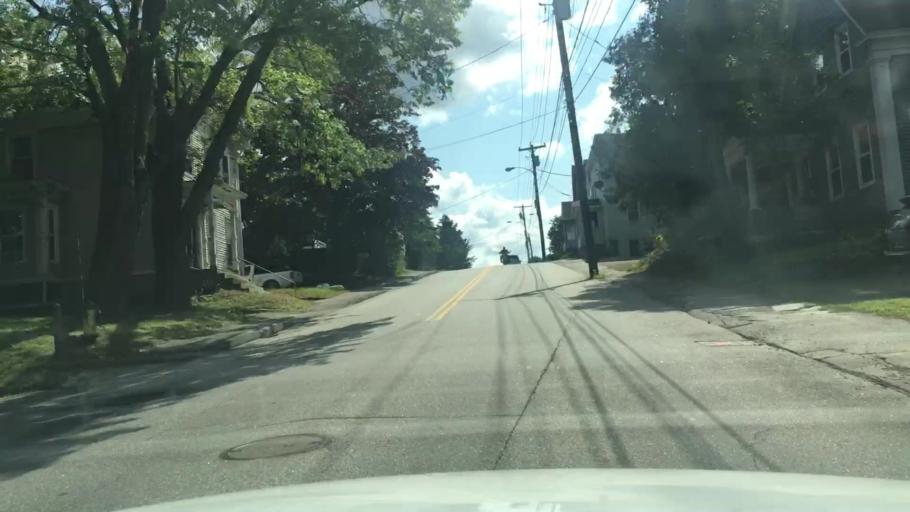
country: US
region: Maine
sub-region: Kennebec County
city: Augusta
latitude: 44.3196
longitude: -69.7756
